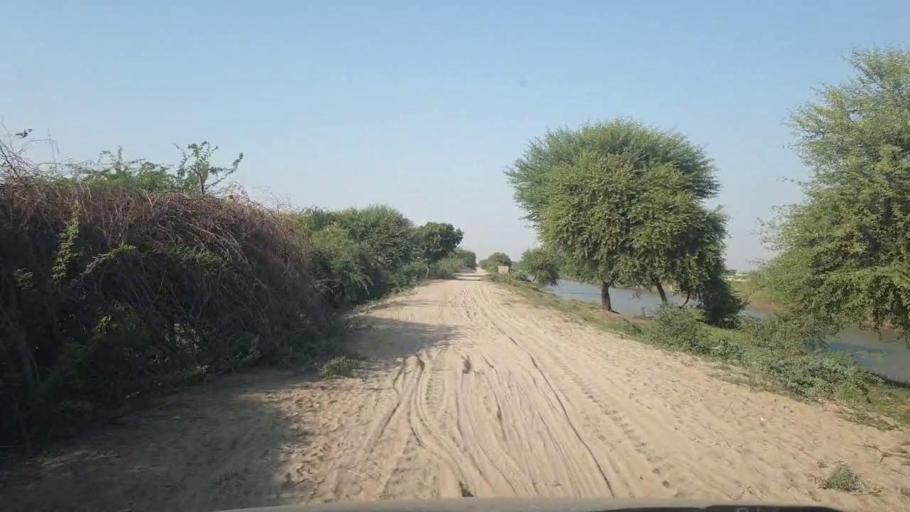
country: PK
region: Sindh
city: Badin
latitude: 24.6444
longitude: 68.8151
